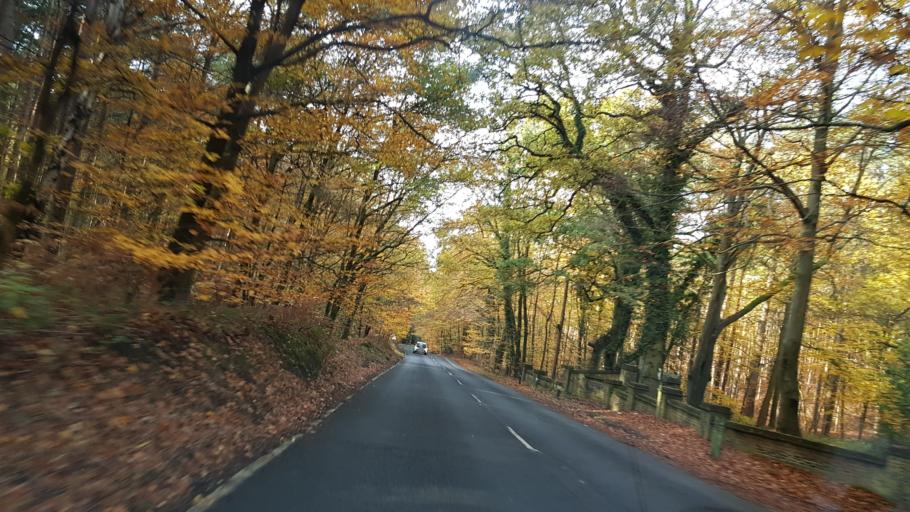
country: GB
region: England
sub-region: Surrey
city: Seale
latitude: 51.2008
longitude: -0.7484
